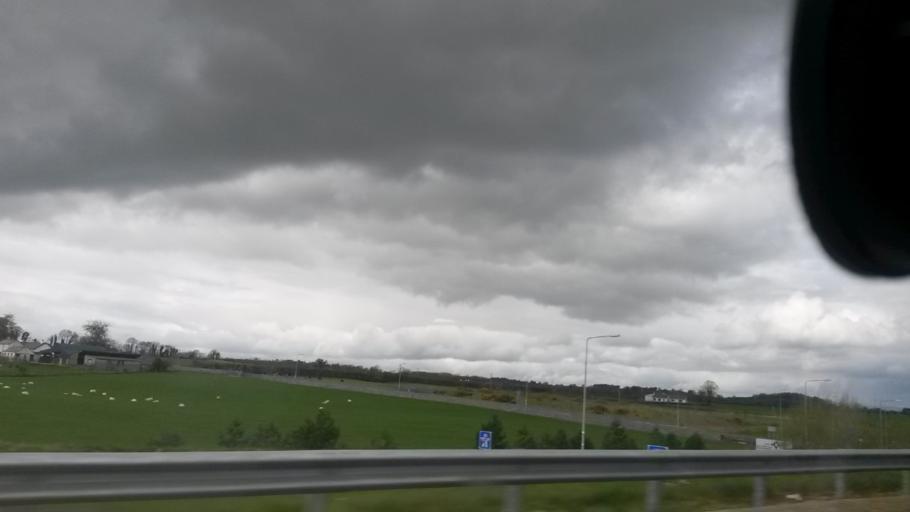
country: IE
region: Leinster
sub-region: Laois
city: Rathdowney
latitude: 52.8650
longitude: -7.4845
